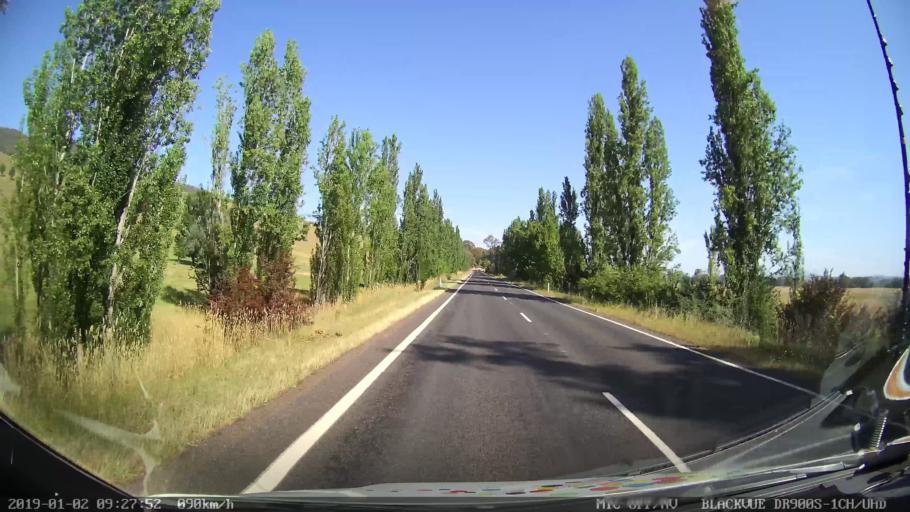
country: AU
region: New South Wales
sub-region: Tumut Shire
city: Tumut
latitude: -35.3572
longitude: 148.2536
